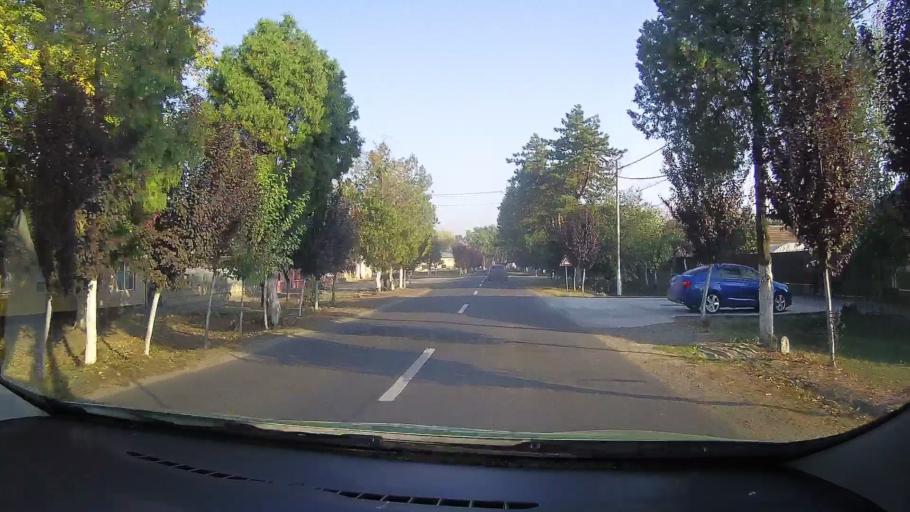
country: RO
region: Arad
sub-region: Comuna Curtici
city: Curtici
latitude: 46.3377
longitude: 21.3082
